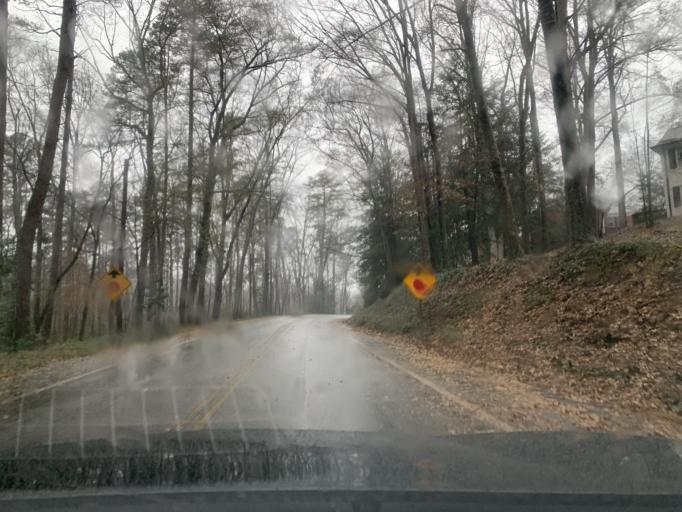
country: US
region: South Carolina
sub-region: Greenville County
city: Greenville
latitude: 34.8423
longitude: -82.3849
